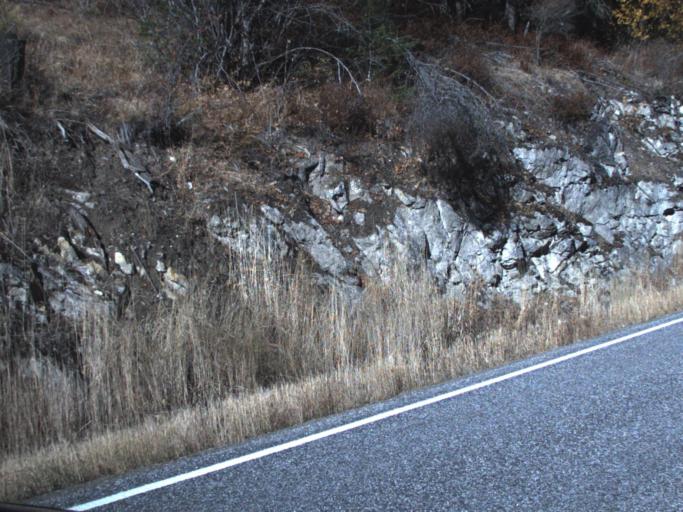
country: CA
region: British Columbia
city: Grand Forks
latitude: 48.9123
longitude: -118.5702
